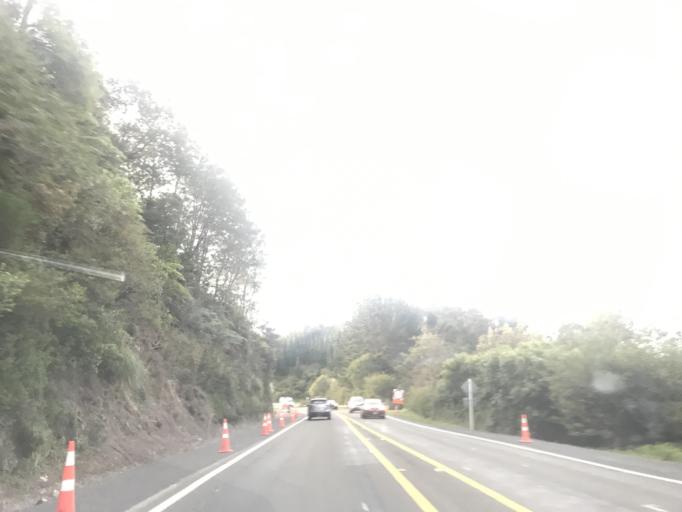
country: NZ
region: Bay of Plenty
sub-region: Western Bay of Plenty District
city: Waihi Beach
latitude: -37.4543
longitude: 175.8930
